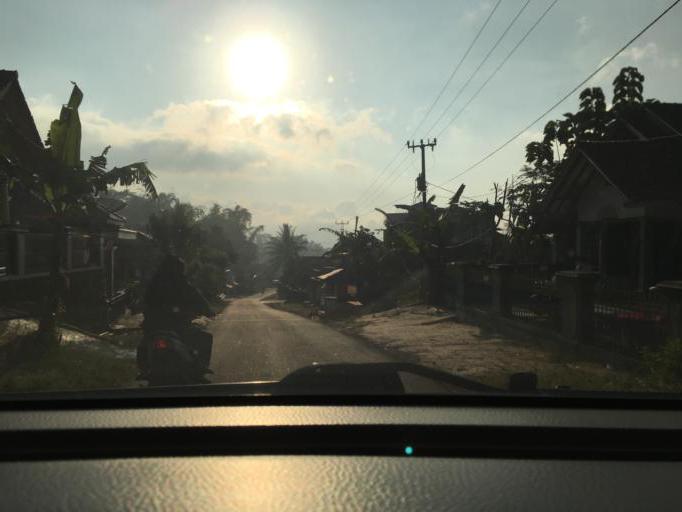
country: ID
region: West Java
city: Maniis
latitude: -7.0384
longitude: 108.3168
